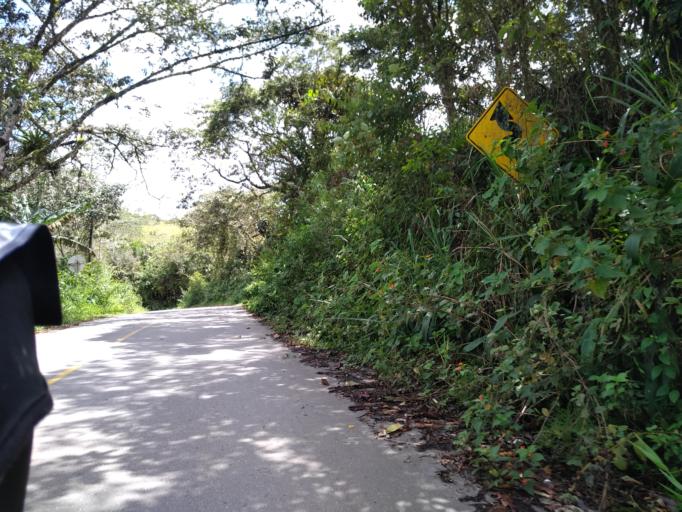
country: CO
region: Santander
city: Oiba
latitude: 6.1877
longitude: -73.1808
